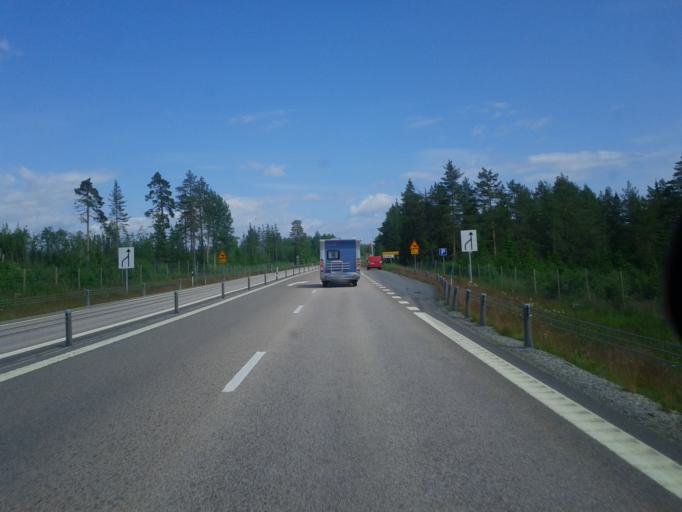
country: SE
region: Vaesternorrland
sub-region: OErnskoeldsviks Kommun
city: Husum
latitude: 63.4788
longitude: 19.2936
